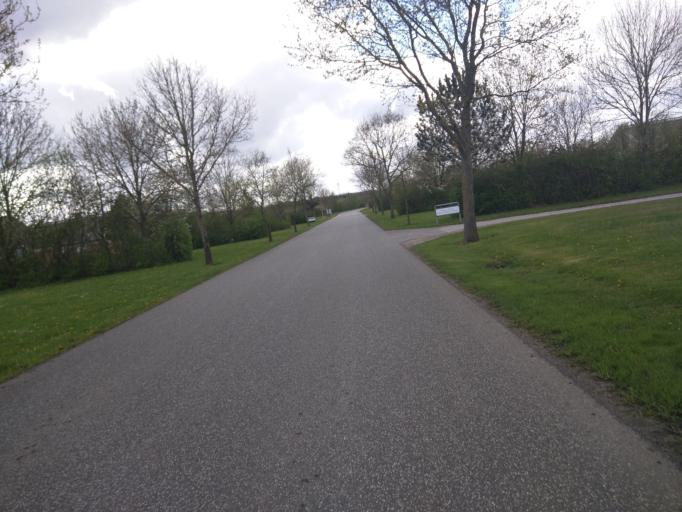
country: DK
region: Central Jutland
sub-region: Viborg Kommune
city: Bjerringbro
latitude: 56.4894
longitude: 9.5800
